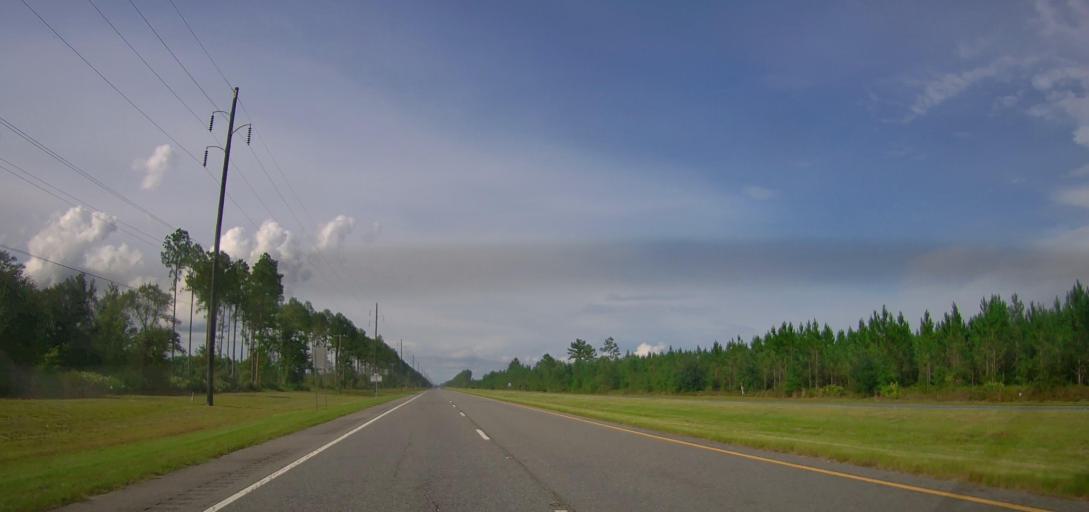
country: US
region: Georgia
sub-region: Wayne County
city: Jesup
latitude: 31.5331
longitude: -81.9829
